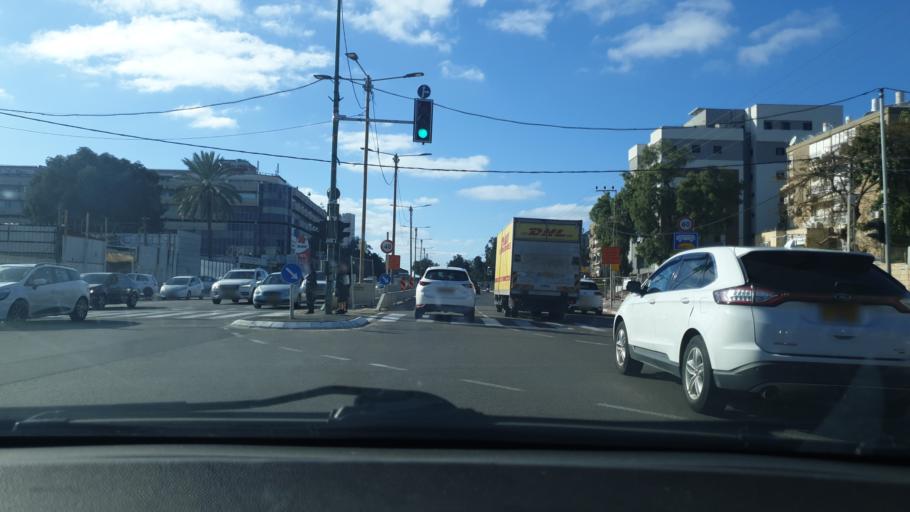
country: IL
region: Tel Aviv
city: Yafo
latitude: 32.0406
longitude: 34.7749
